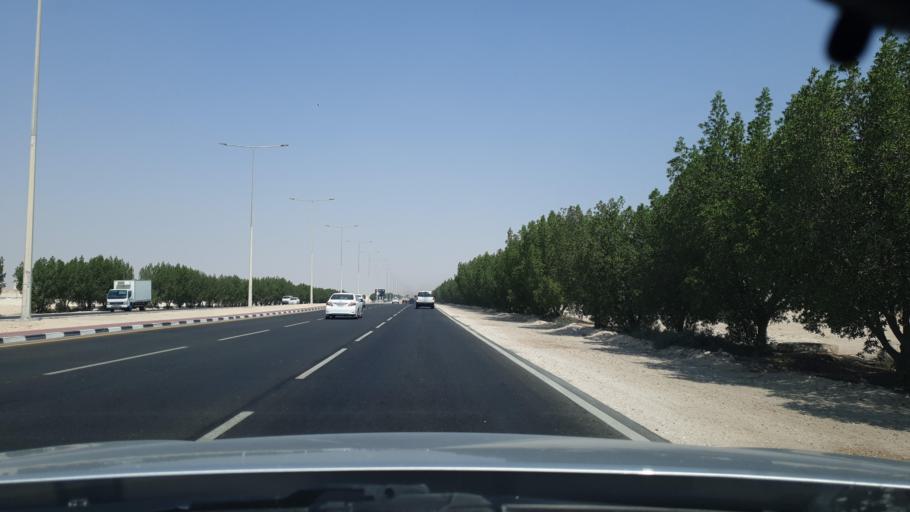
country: QA
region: Al Khawr
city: Al Khawr
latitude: 25.6947
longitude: 51.5017
